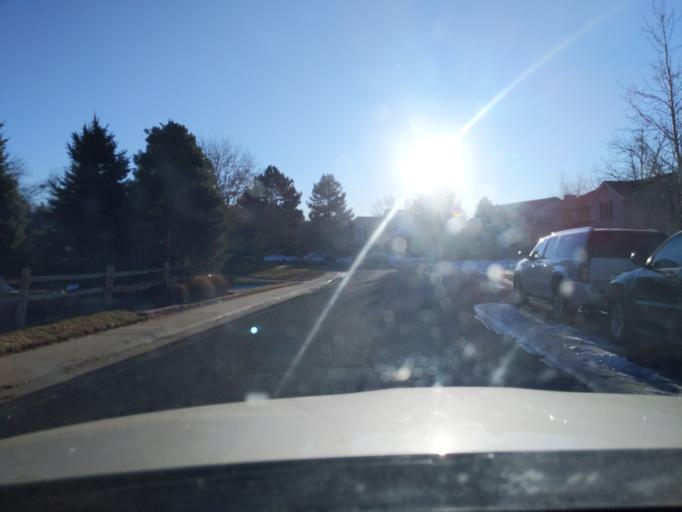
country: US
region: Colorado
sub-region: Douglas County
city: Acres Green
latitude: 39.5670
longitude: -104.8889
